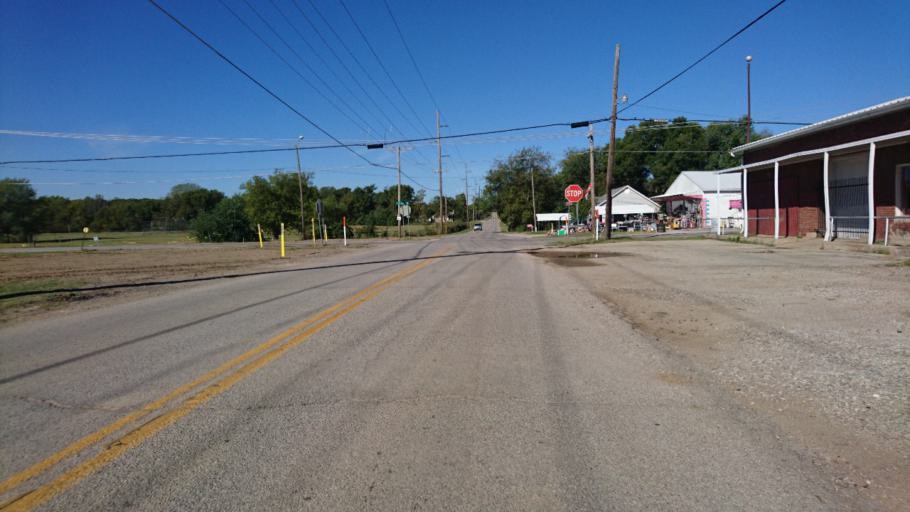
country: US
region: Oklahoma
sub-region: Rogers County
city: Catoosa
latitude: 36.1480
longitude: -95.7792
